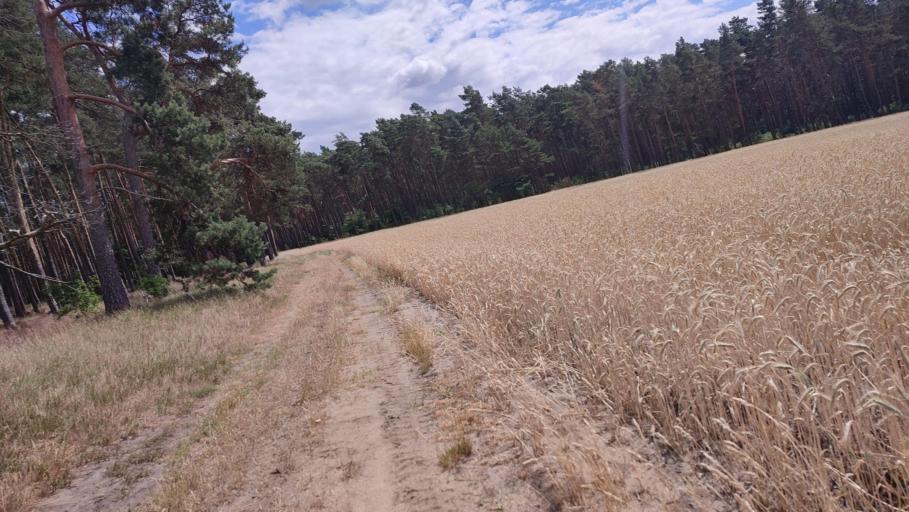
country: DE
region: Lower Saxony
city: Hitzacker
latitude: 53.2129
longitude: 11.0671
